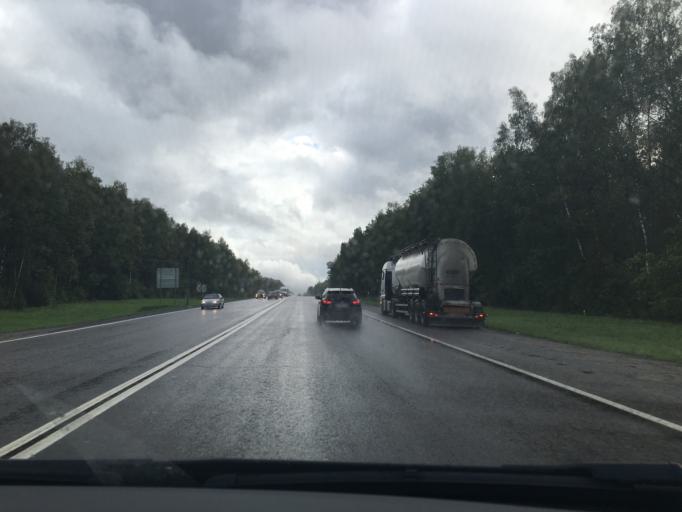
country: RU
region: Kaluga
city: Balabanovo
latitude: 55.1474
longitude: 36.6608
